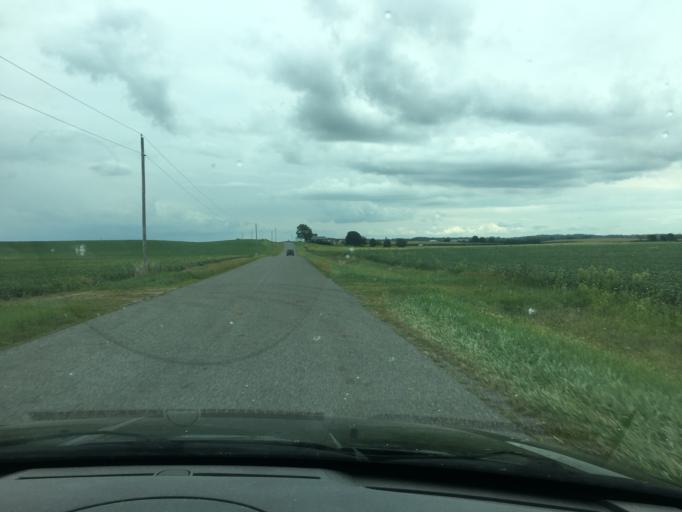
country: US
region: Ohio
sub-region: Logan County
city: West Liberty
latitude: 40.2111
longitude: -83.7070
